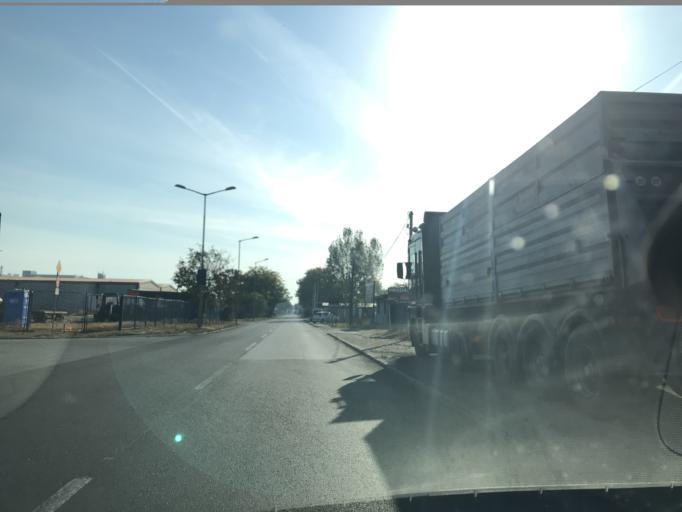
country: RS
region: Autonomna Pokrajina Vojvodina
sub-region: Juznobacki Okrug
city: Novi Sad
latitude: 45.2684
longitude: 19.8514
